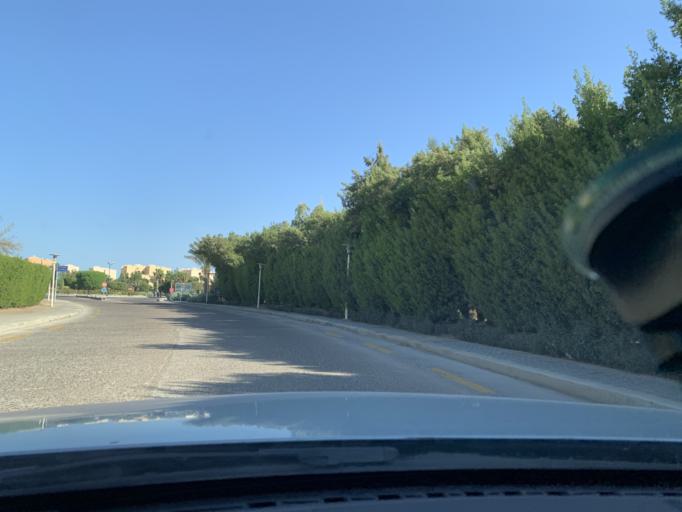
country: EG
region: Red Sea
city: El Gouna
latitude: 27.4044
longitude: 33.6715
